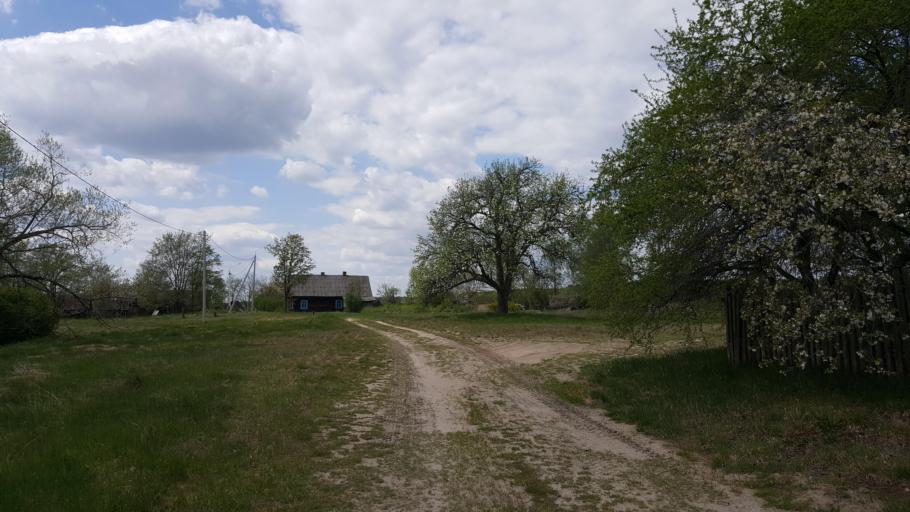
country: BY
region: Brest
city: Zhabinka
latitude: 52.4122
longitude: 24.0909
